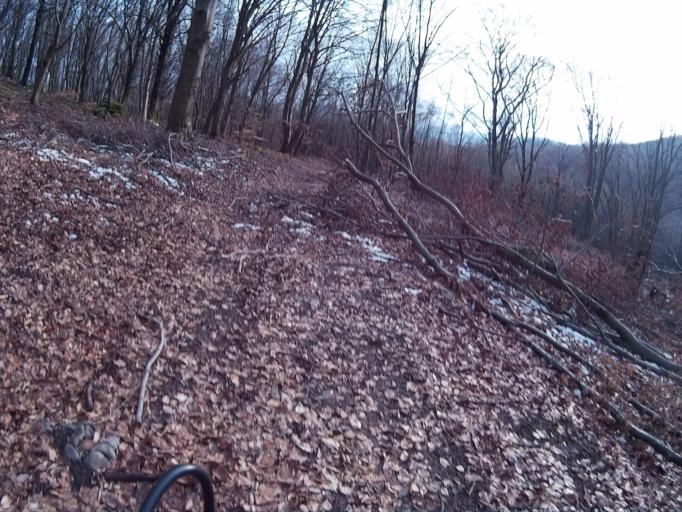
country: HU
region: Borsod-Abauj-Zemplen
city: Gonc
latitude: 48.4050
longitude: 21.3497
